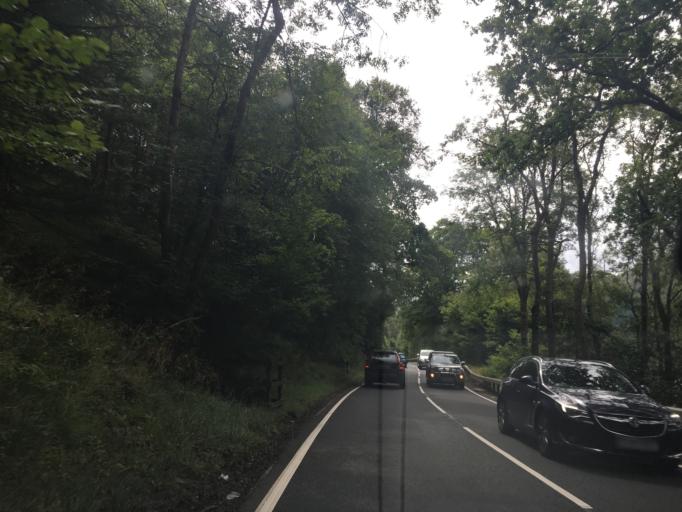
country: GB
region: Scotland
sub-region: Stirling
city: Callander
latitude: 56.2730
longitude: -4.2826
